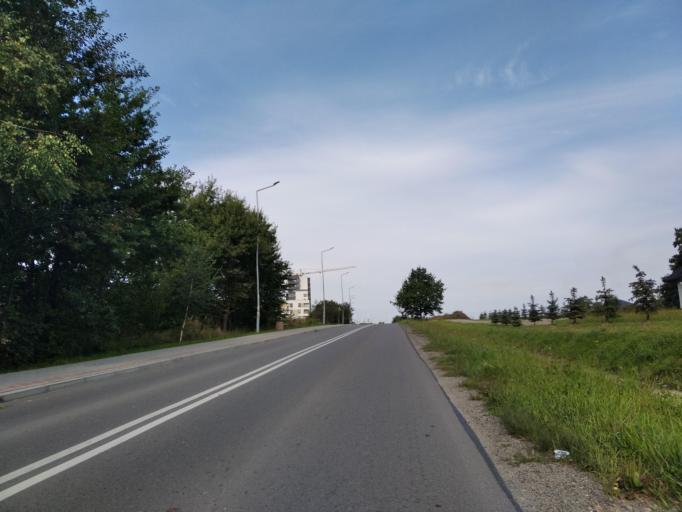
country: PL
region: Subcarpathian Voivodeship
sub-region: Powiat ropczycko-sedziszowski
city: Ropczyce
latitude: 50.0607
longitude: 21.6138
